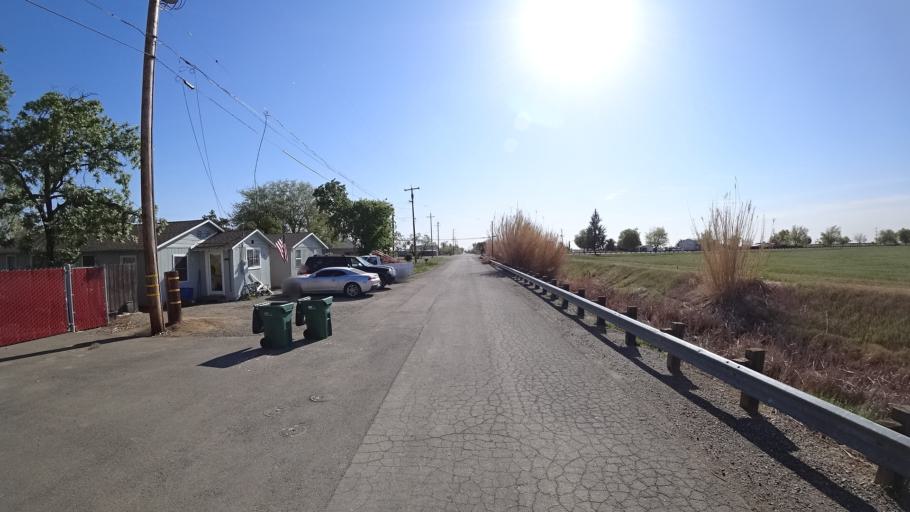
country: US
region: California
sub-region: Glenn County
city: Willows
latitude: 39.5096
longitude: -122.1954
